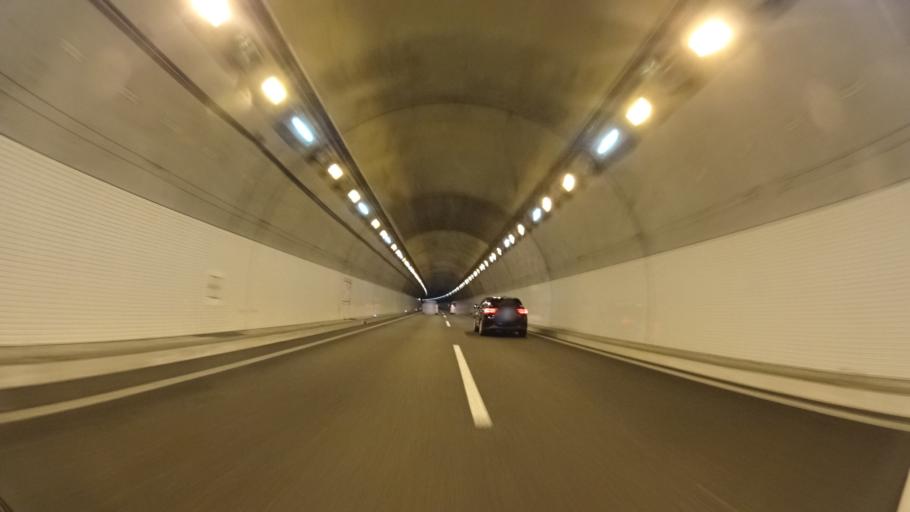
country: JP
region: Ehime
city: Saijo
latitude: 33.9068
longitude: 133.2144
